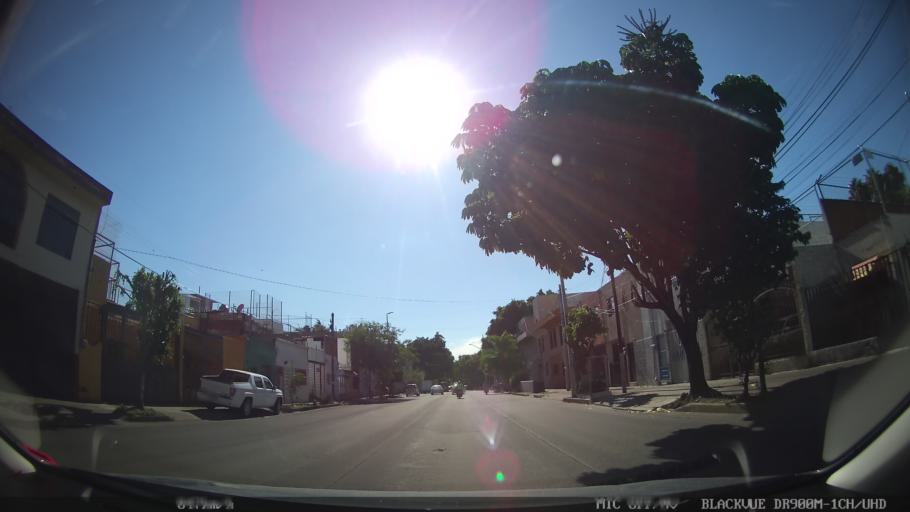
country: MX
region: Jalisco
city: Tlaquepaque
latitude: 20.6656
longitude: -103.3069
